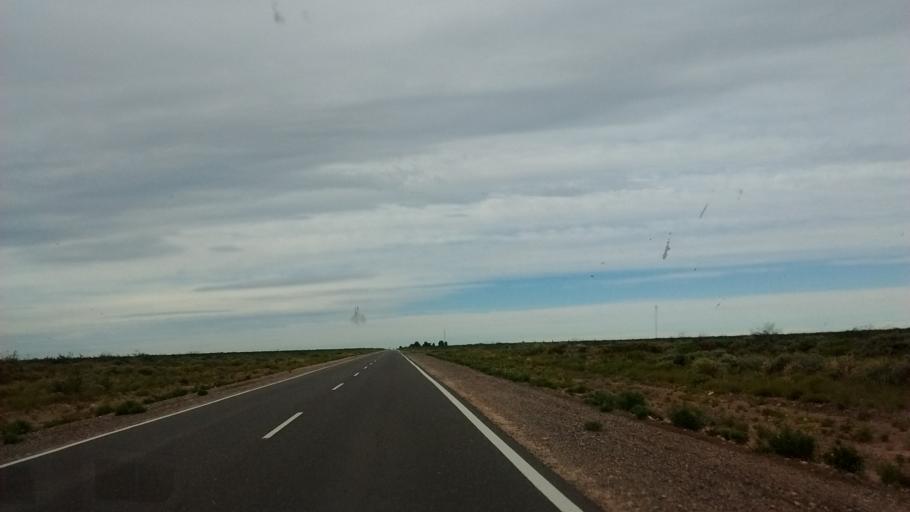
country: AR
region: Rio Negro
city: Contraalmirante Cordero
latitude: -38.3847
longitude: -68.0250
